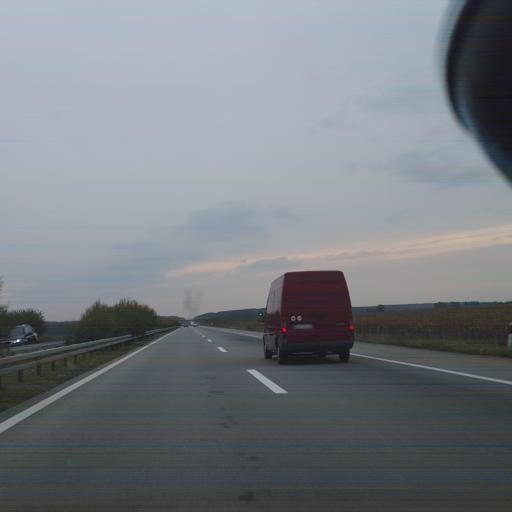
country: RS
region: Autonomna Pokrajina Vojvodina
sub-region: Juznobacki Okrug
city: Sremski Karlovci
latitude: 45.2699
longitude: 19.9492
